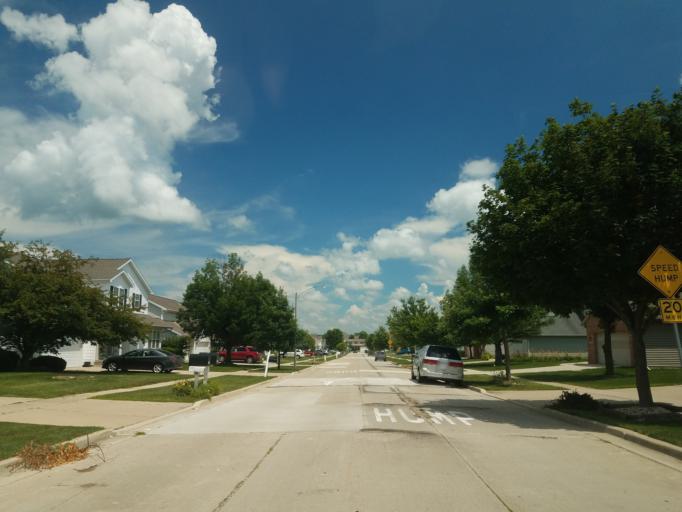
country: US
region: Illinois
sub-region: McLean County
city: Normal
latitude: 40.4967
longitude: -88.9229
